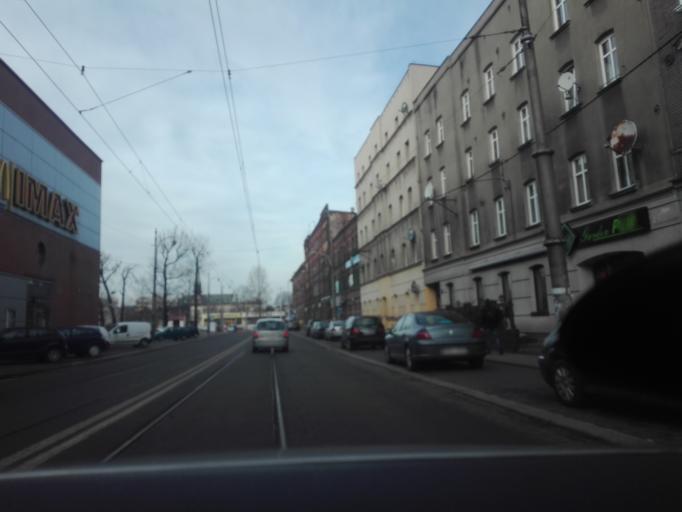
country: PL
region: Silesian Voivodeship
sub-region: Katowice
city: Katowice
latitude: 50.2628
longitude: 19.0064
